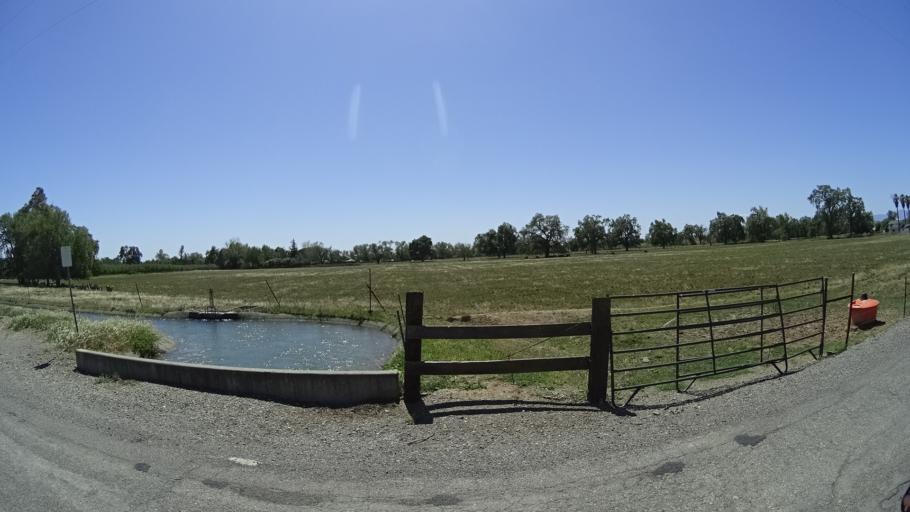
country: US
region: California
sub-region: Glenn County
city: Orland
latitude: 39.7953
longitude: -122.2414
